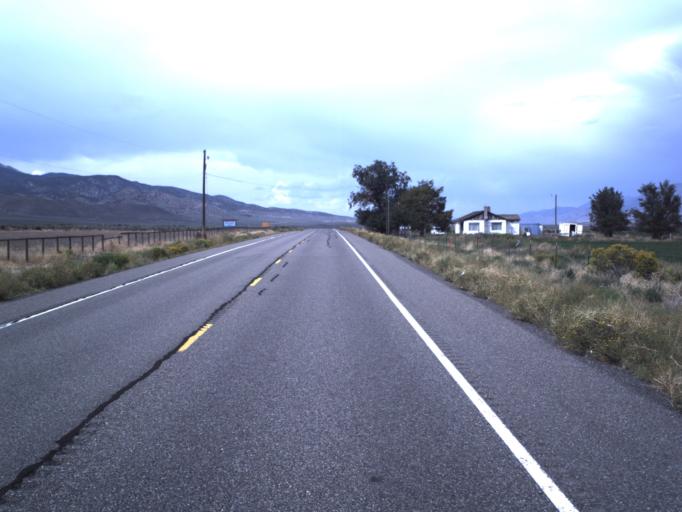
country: US
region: Utah
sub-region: Piute County
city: Junction
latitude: 38.2537
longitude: -112.2204
